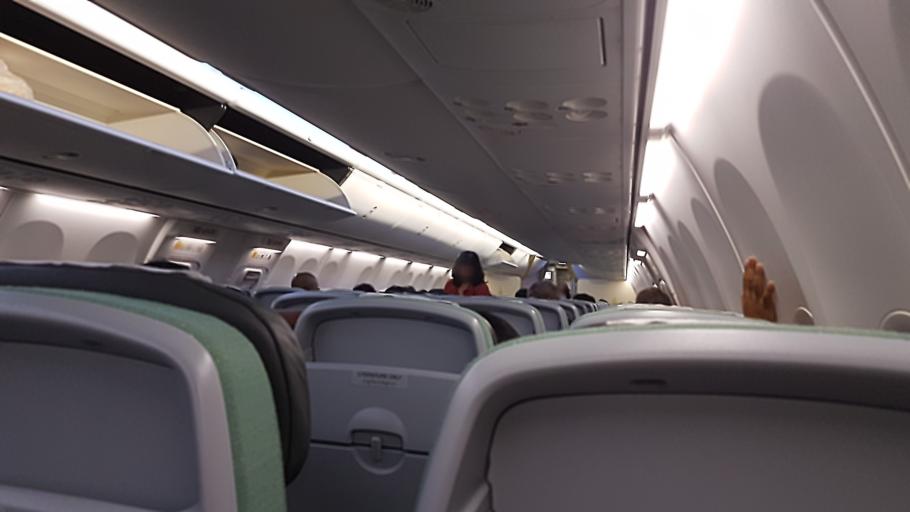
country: MM
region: Mandalay
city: Pyinmana
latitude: 19.6159
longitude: 96.2113
